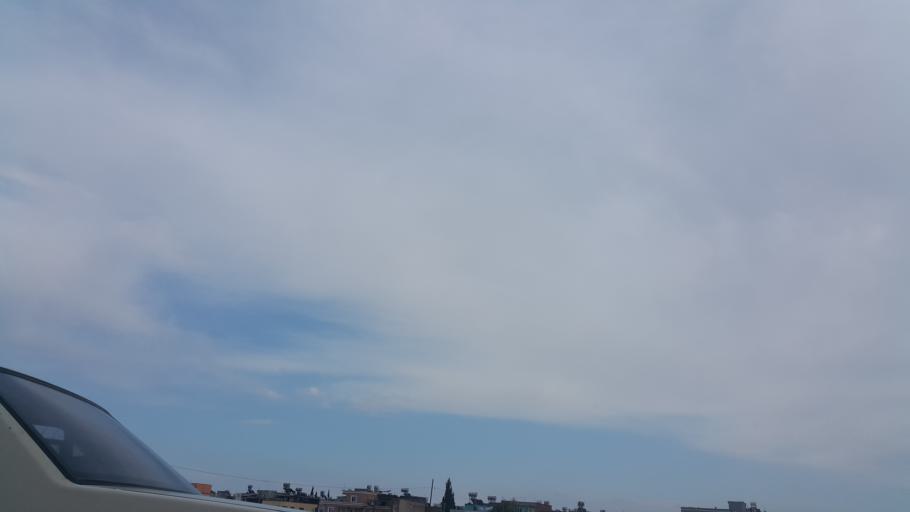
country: TR
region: Mersin
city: Tarsus
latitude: 36.9153
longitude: 34.9191
